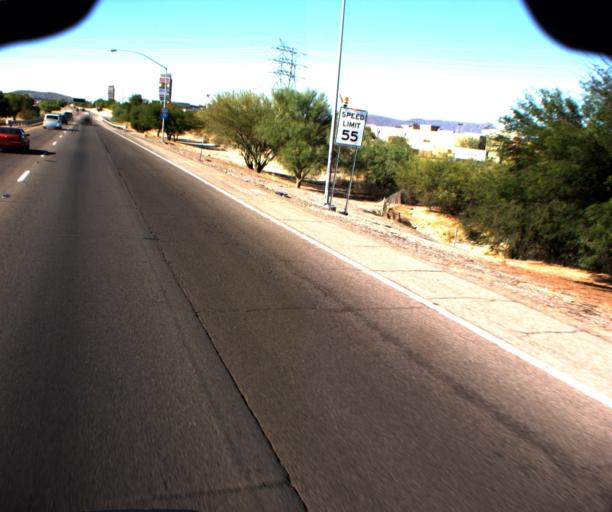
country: US
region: Arizona
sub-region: Pima County
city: Drexel Heights
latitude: 32.1576
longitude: -110.9863
